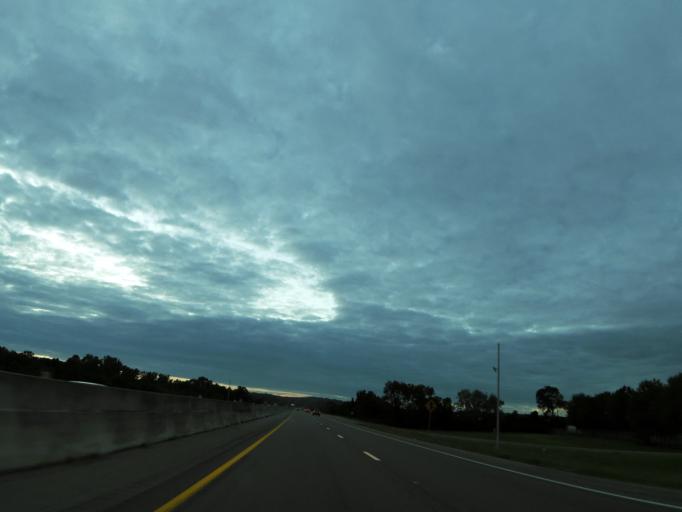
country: US
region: Tennessee
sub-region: Davidson County
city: Nashville
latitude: 36.1885
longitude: -86.8626
